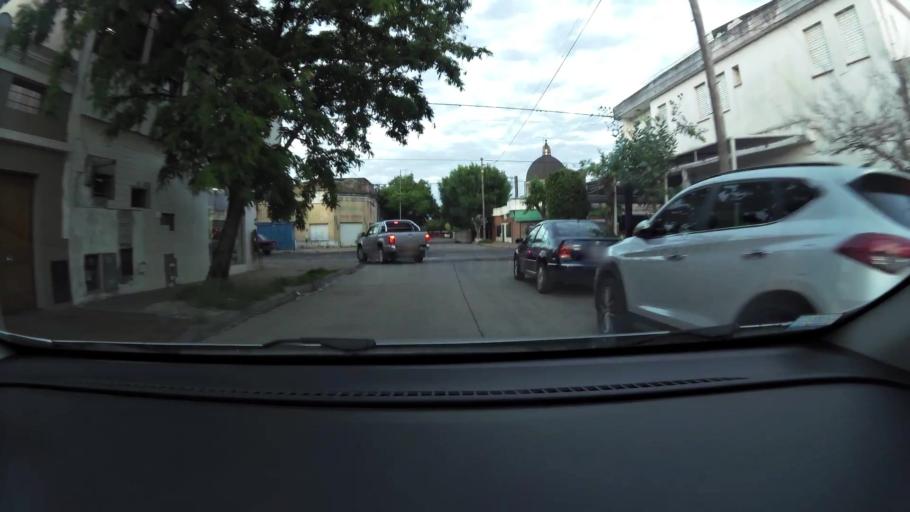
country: AR
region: Buenos Aires
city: San Nicolas de los Arroyos
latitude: -33.3239
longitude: -60.2261
